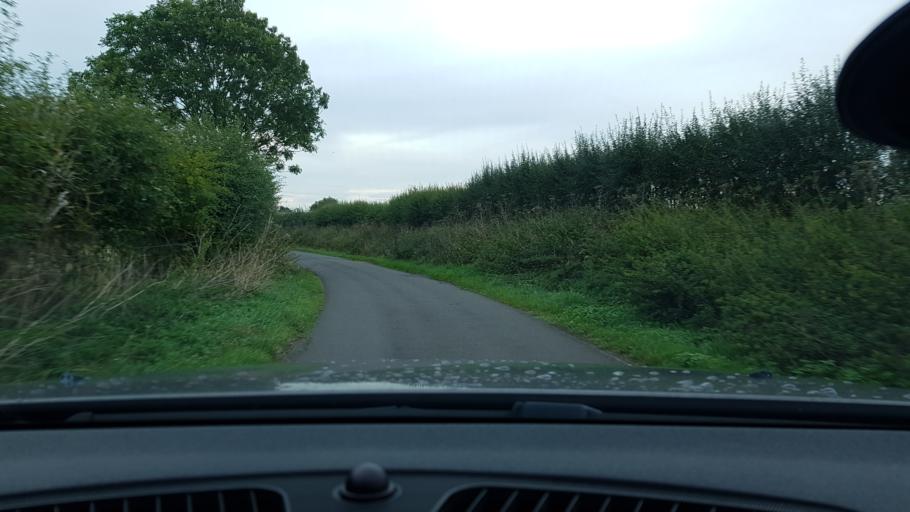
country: GB
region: England
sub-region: West Berkshire
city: Kintbury
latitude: 51.3959
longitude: -1.4095
